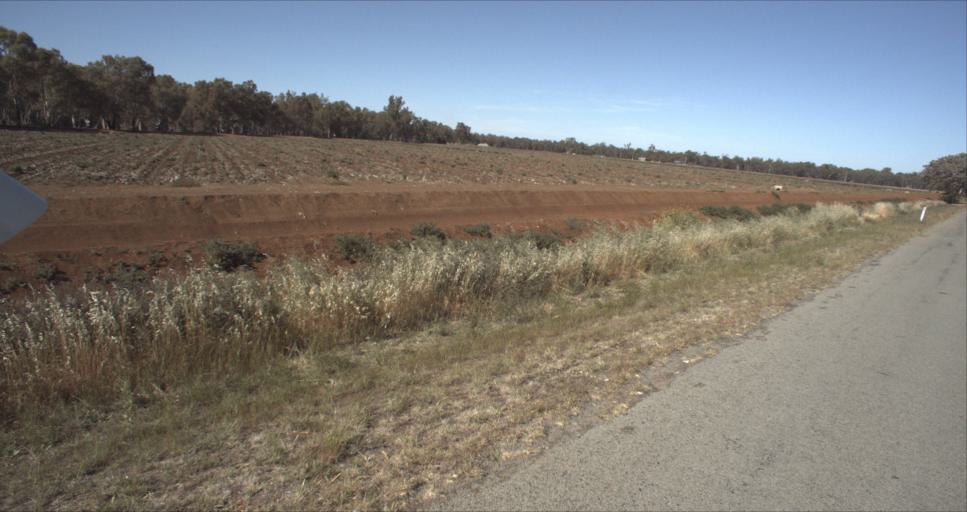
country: AU
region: New South Wales
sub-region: Leeton
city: Leeton
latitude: -34.6047
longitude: 146.2631
